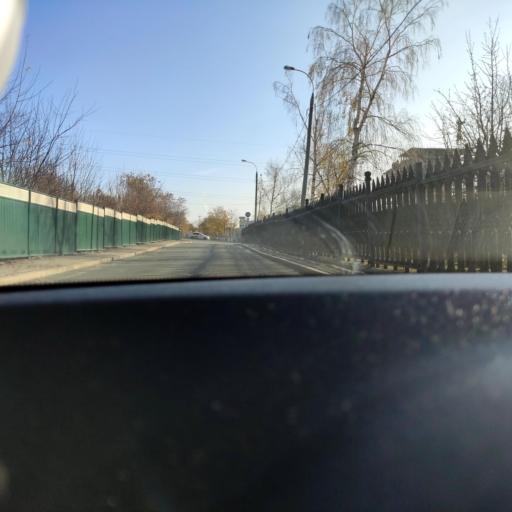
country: RU
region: Samara
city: Samara
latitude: 53.2285
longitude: 50.1737
